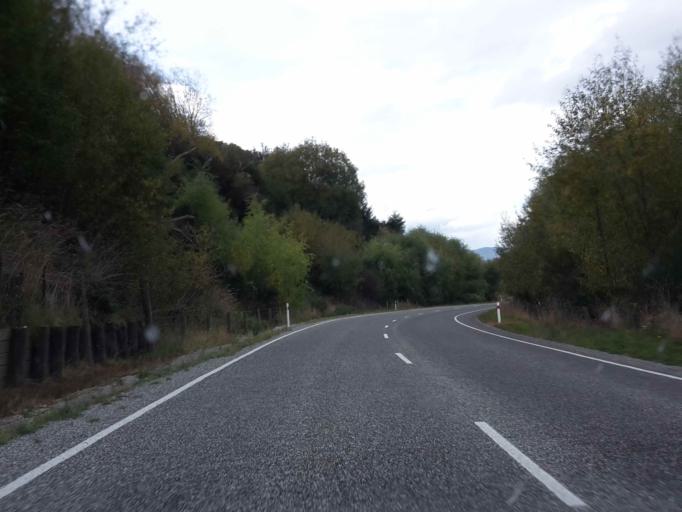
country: NZ
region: Otago
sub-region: Queenstown-Lakes District
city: Wanaka
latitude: -44.7512
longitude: 169.1161
